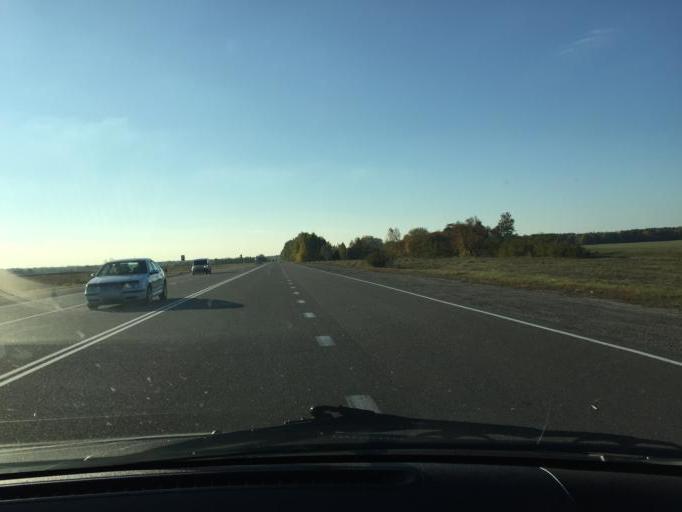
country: BY
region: Brest
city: Horad Luninyets
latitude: 52.3172
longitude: 26.6175
